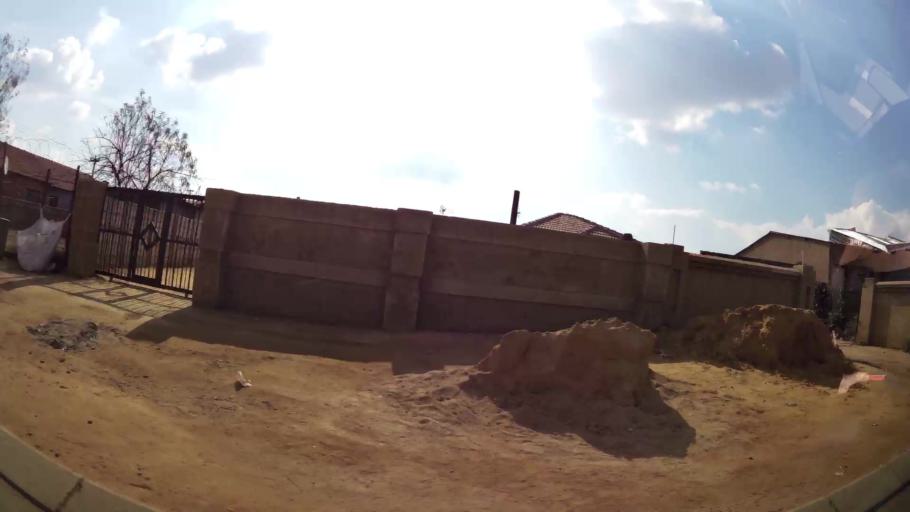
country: ZA
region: Gauteng
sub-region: Ekurhuleni Metropolitan Municipality
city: Springs
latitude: -26.1210
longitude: 28.4838
